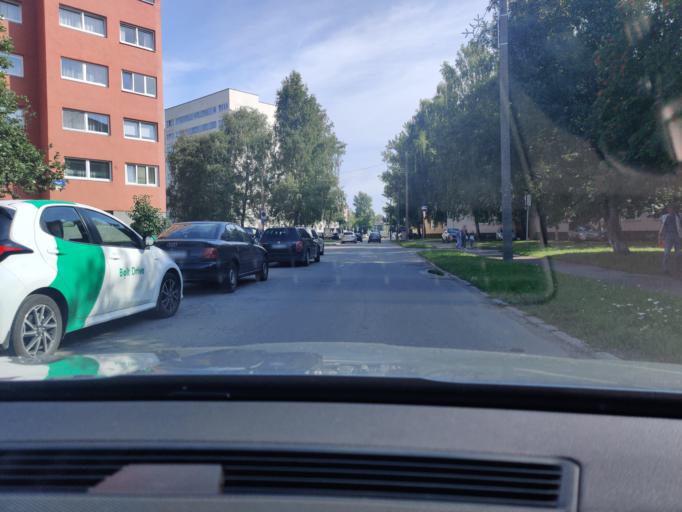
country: EE
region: Harju
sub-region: Tallinna linn
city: Tallinn
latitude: 59.4474
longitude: 24.6952
